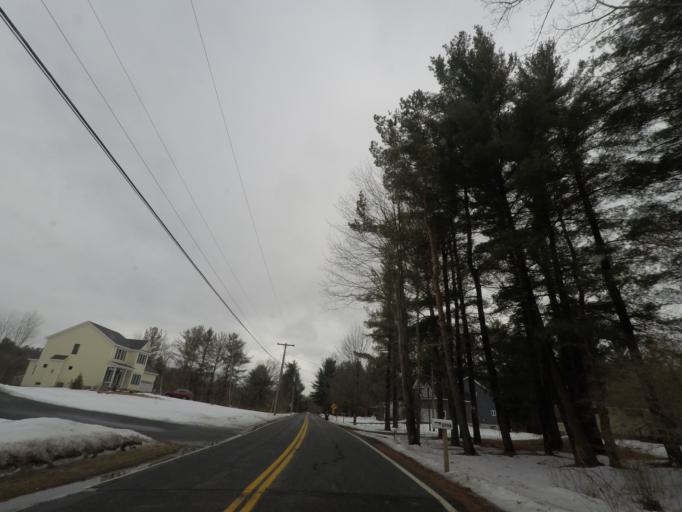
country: US
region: New York
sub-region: Schenectady County
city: Rotterdam
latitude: 42.7454
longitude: -73.9644
